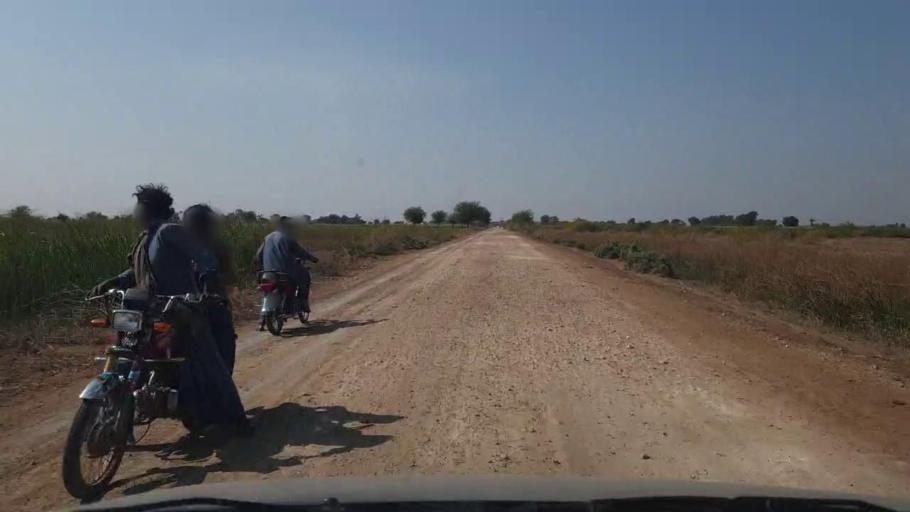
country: PK
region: Sindh
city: Samaro
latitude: 25.1882
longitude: 69.3582
